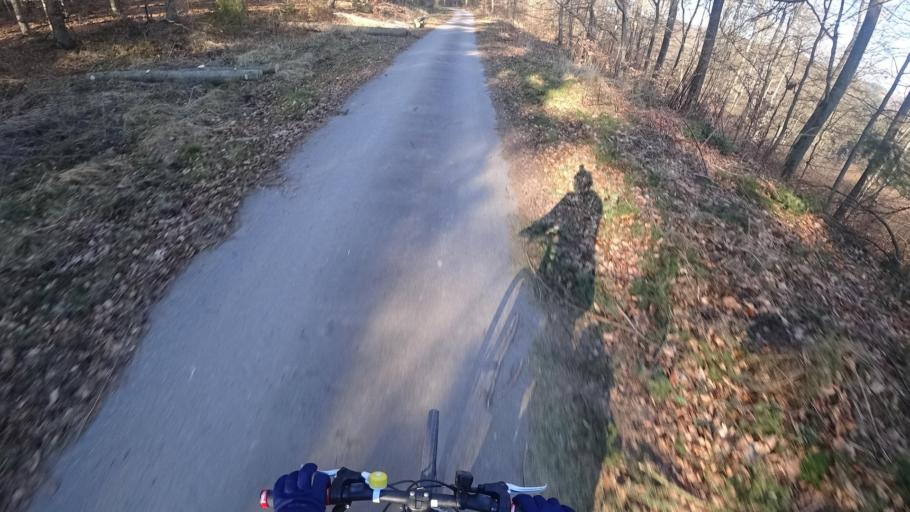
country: DE
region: Rheinland-Pfalz
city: Waldesch
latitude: 50.2518
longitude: 7.5261
